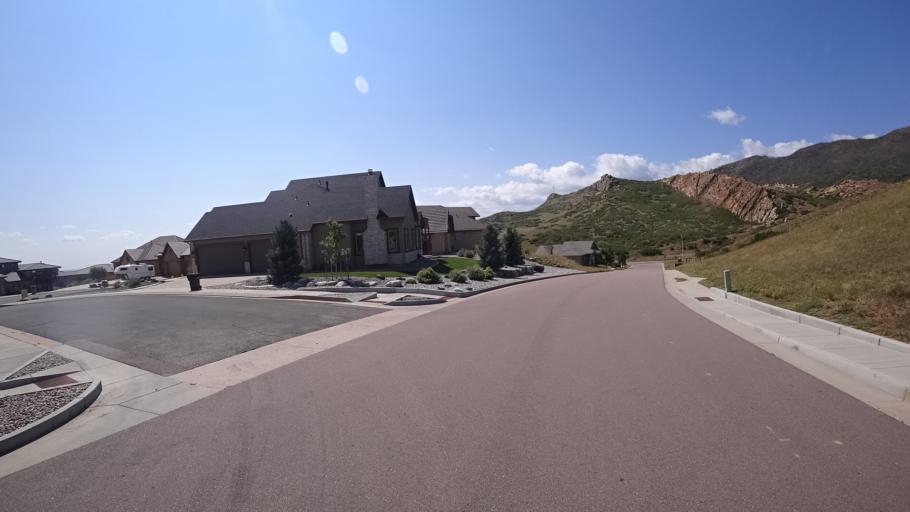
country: US
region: Colorado
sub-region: El Paso County
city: Manitou Springs
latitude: 38.9171
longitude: -104.8774
